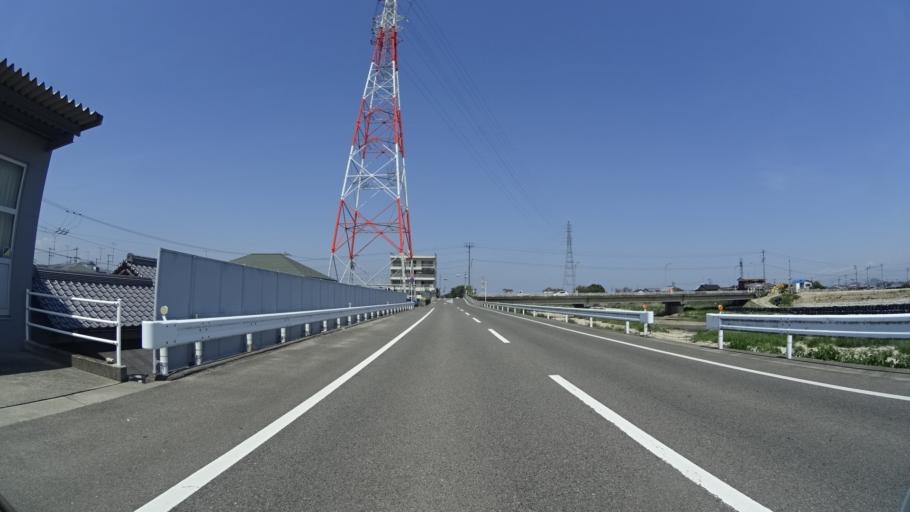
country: JP
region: Ehime
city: Hojo
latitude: 34.0384
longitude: 132.9762
